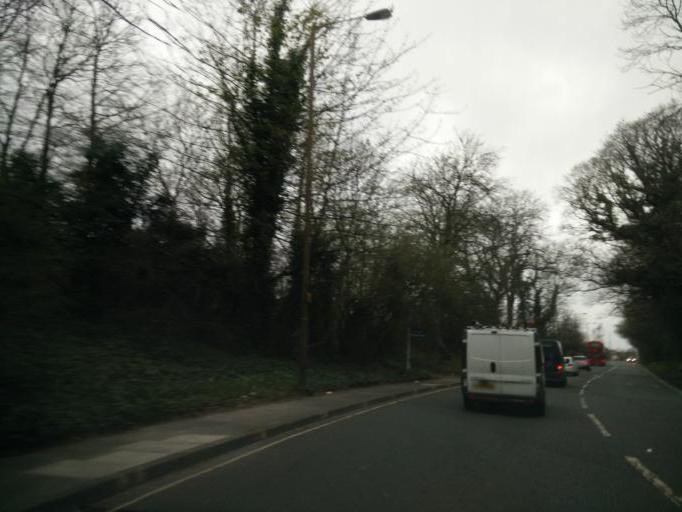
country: GB
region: England
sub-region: County Durham
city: Durham
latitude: 54.7729
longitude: -1.5877
